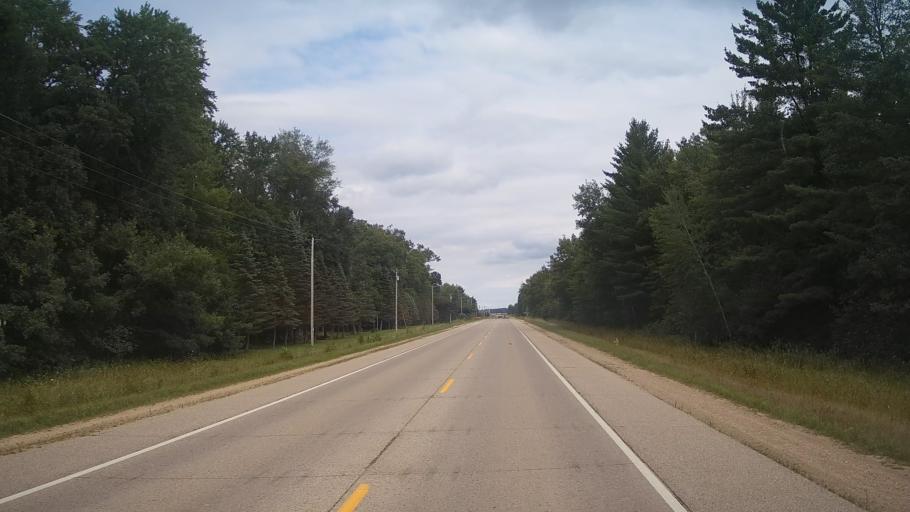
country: US
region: Wisconsin
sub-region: Waushara County
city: Redgranite
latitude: 44.0375
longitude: -89.0773
